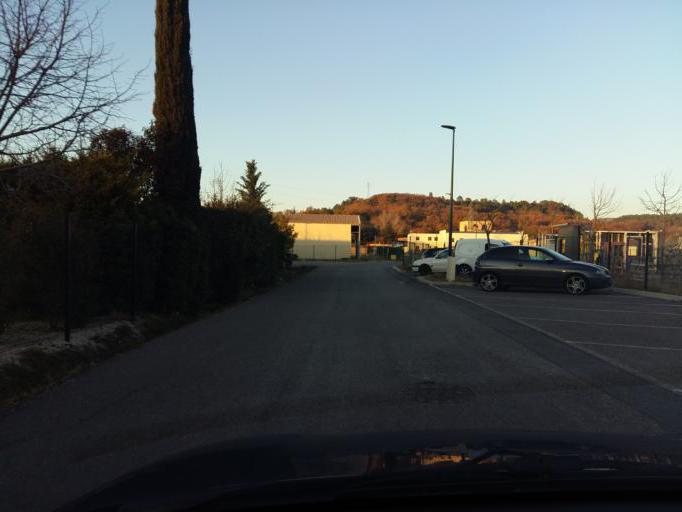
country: FR
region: Rhone-Alpes
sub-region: Departement de la Drome
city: La Garde-Adhemar
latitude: 44.4167
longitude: 4.8060
